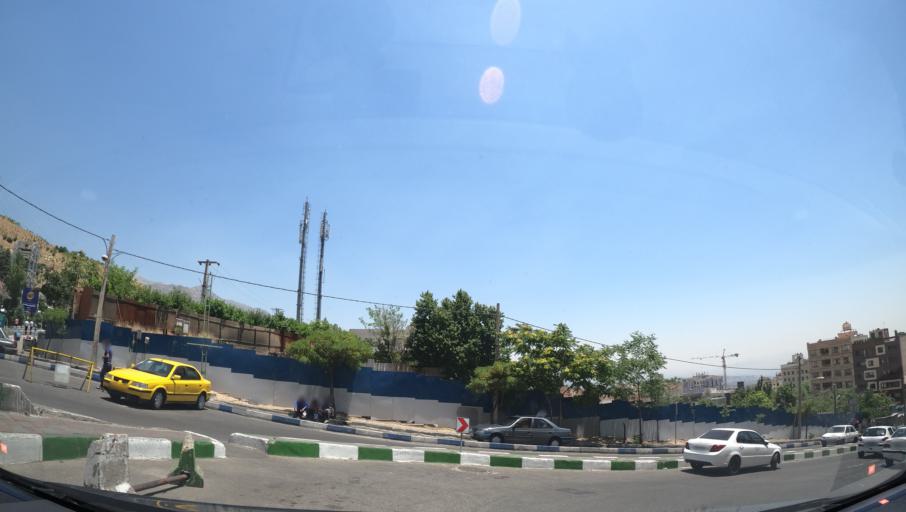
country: IR
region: Tehran
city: Tajrish
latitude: 35.8128
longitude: 51.3985
